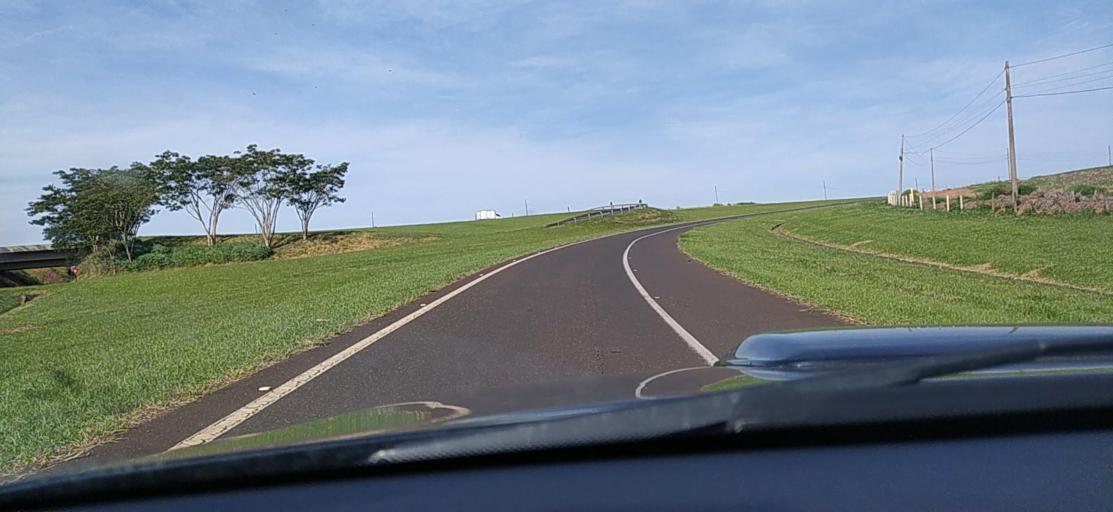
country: BR
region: Sao Paulo
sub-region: Pindorama
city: Pindorama
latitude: -21.2066
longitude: -48.9313
